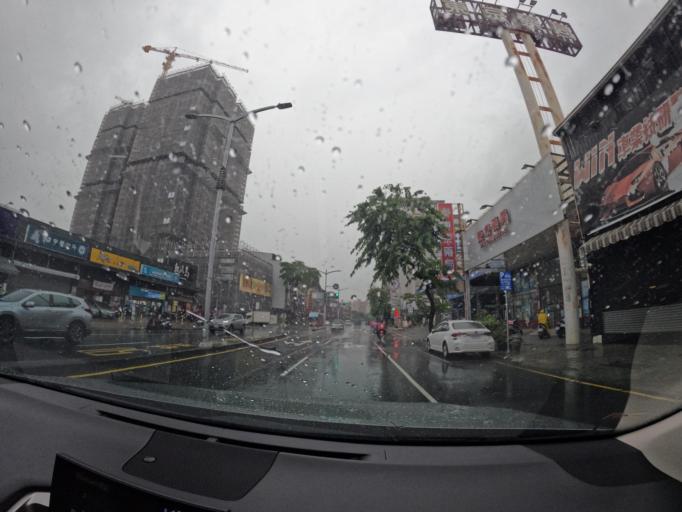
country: TW
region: Kaohsiung
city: Kaohsiung
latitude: 22.6624
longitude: 120.3220
